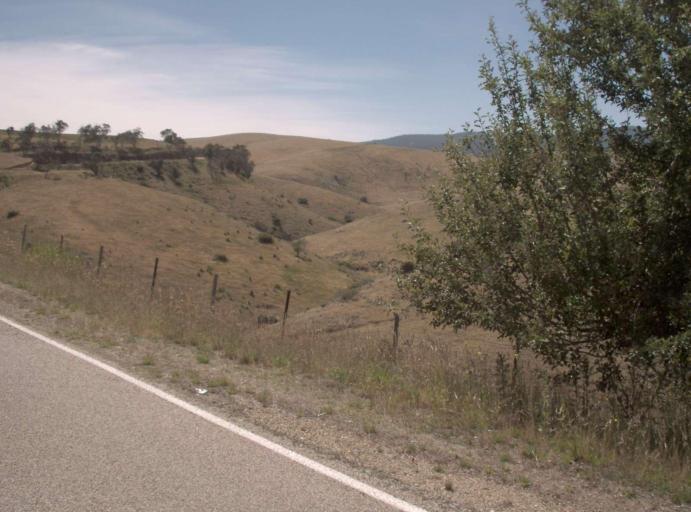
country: AU
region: Victoria
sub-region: Alpine
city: Mount Beauty
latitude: -37.0647
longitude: 147.6086
